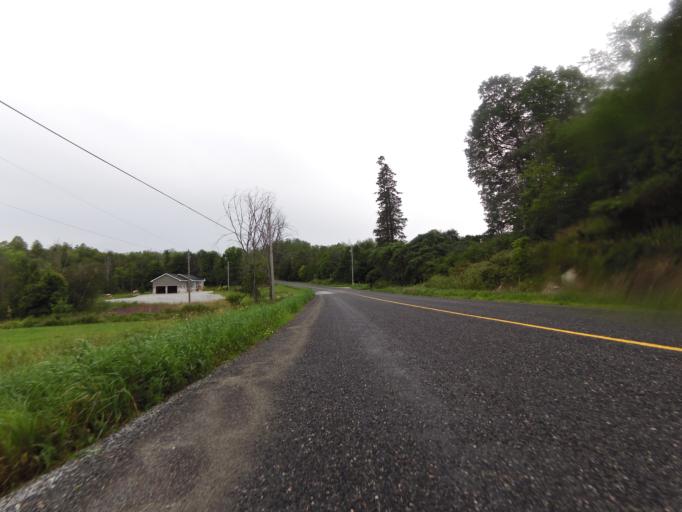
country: CA
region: Ontario
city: Perth
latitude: 44.9156
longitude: -76.4841
